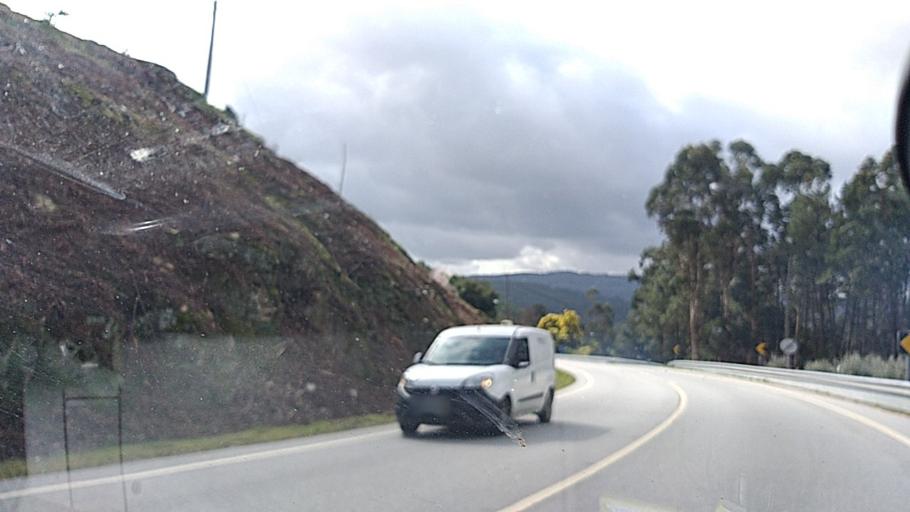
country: PT
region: Viseu
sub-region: Mangualde
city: Mangualde
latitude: 40.6535
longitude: -7.7331
